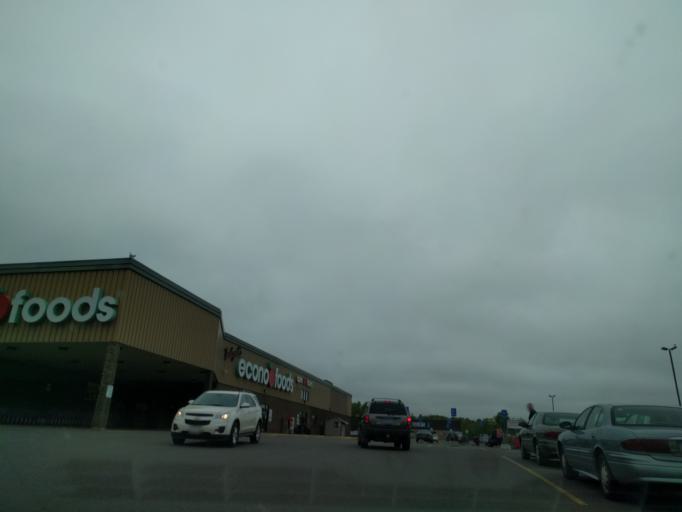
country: US
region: Michigan
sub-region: Marquette County
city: Trowbridge Park
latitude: 46.5427
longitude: -87.4231
